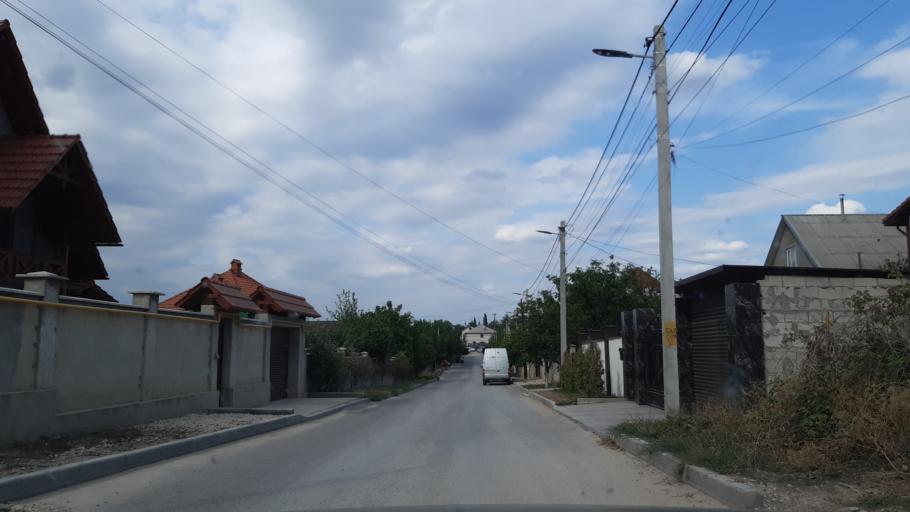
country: MD
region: Chisinau
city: Vatra
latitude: 47.0470
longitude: 28.7370
